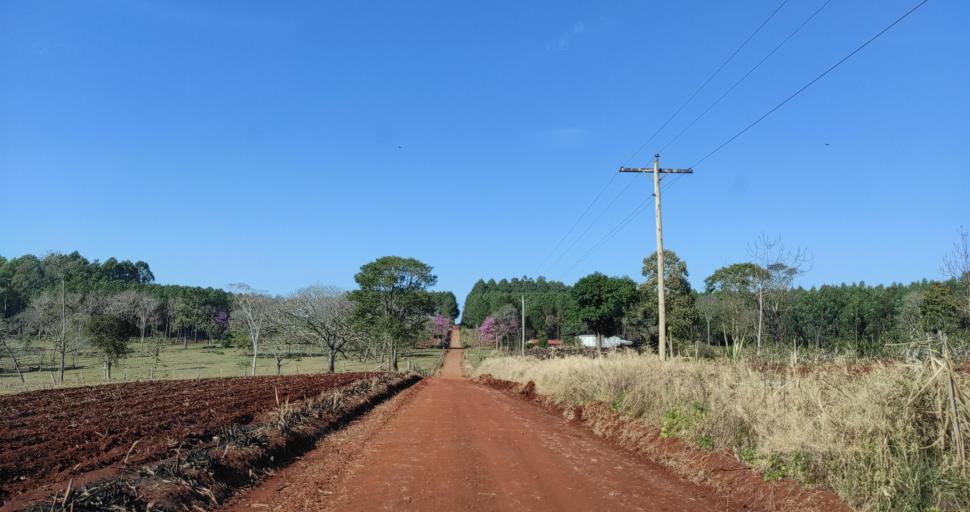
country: AR
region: Misiones
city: Capiovi
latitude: -26.8839
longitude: -55.0374
